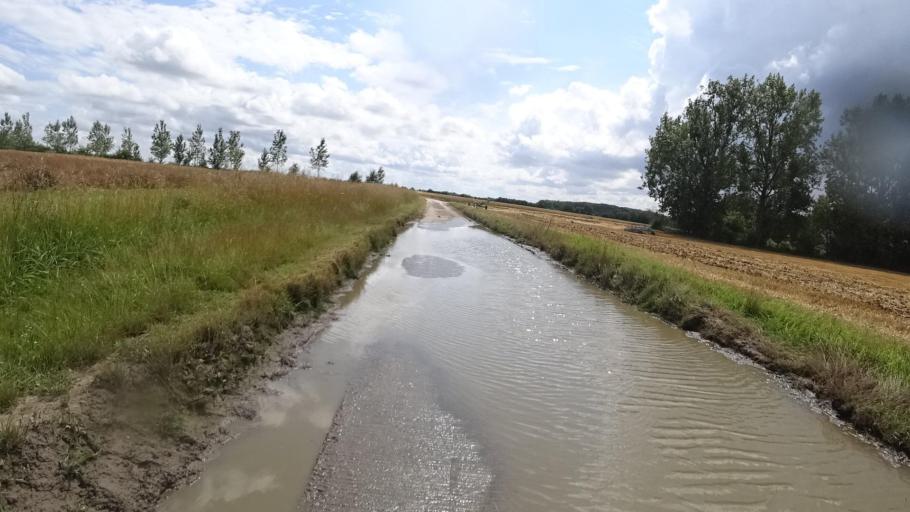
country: BE
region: Wallonia
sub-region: Province du Brabant Wallon
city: Court-Saint-Etienne
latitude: 50.5855
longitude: 4.5785
